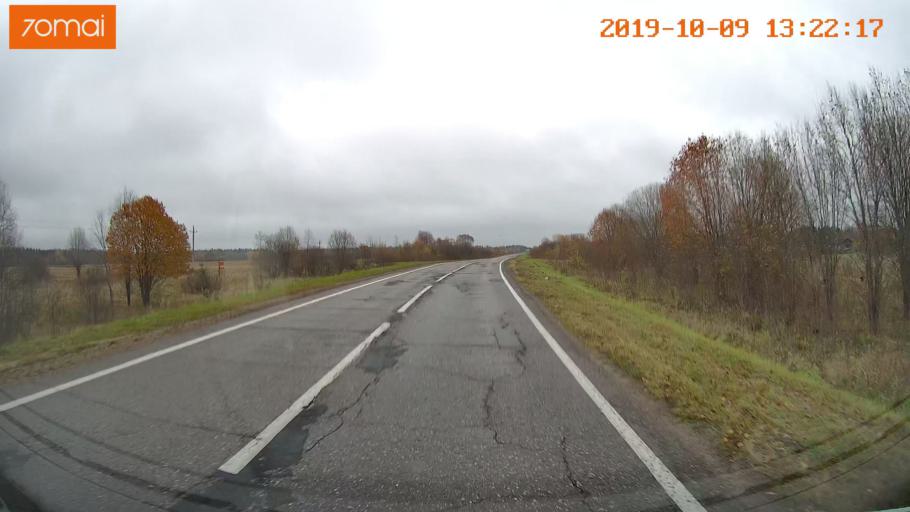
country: RU
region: Jaroslavl
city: Lyubim
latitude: 58.3406
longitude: 40.8618
